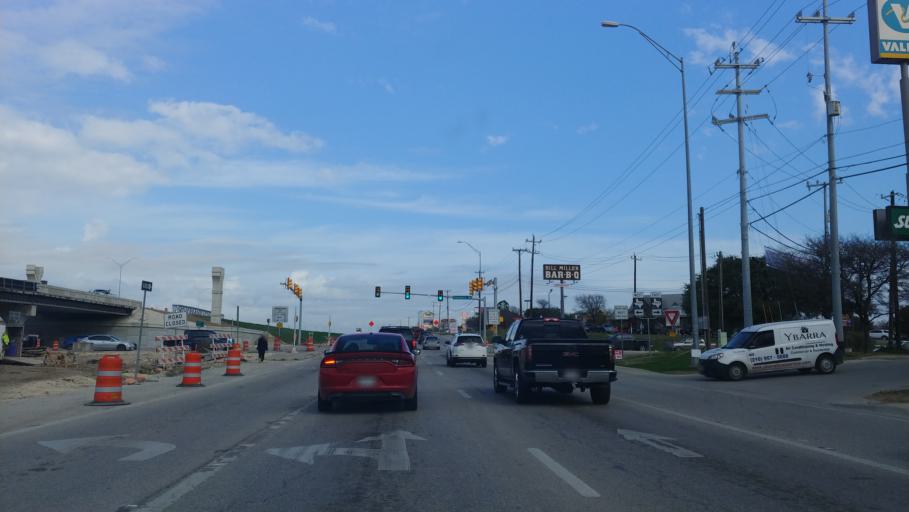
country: US
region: Texas
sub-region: Bexar County
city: Lackland Air Force Base
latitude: 29.4349
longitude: -98.7107
